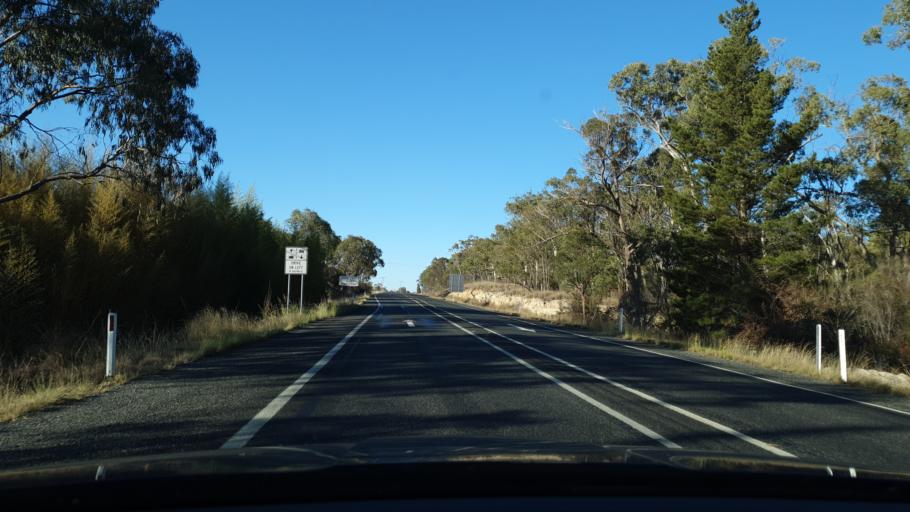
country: AU
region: Queensland
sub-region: Southern Downs
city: Stanthorpe
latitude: -28.6964
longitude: 151.9065
